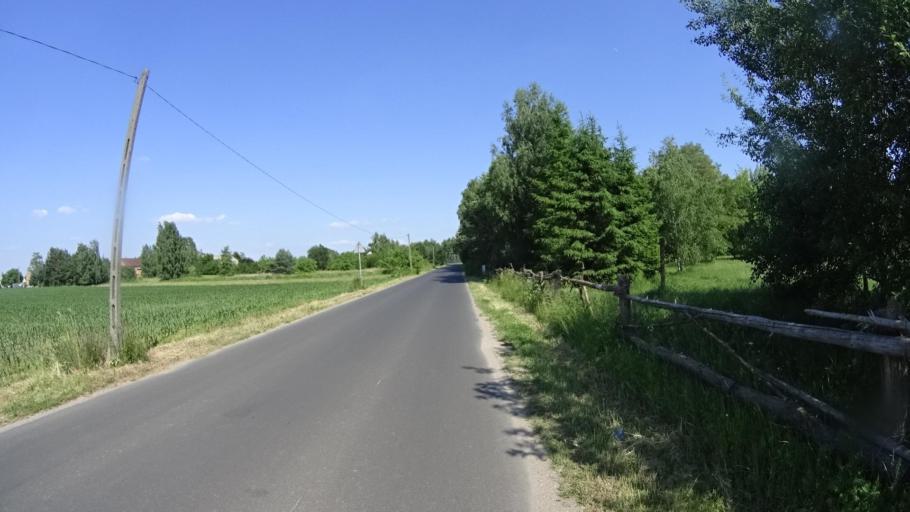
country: PL
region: Masovian Voivodeship
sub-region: Powiat warszawski zachodni
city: Blonie
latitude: 52.1651
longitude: 20.6325
